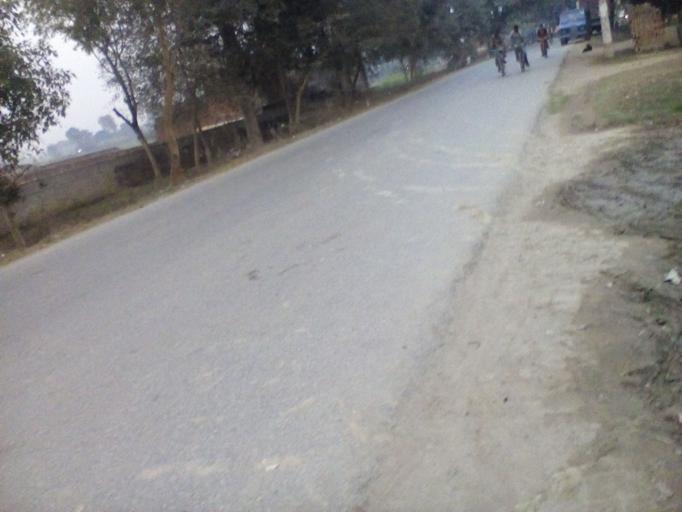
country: IN
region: Uttar Pradesh
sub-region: Varanasi
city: Varanasi
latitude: 25.3170
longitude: 82.8810
